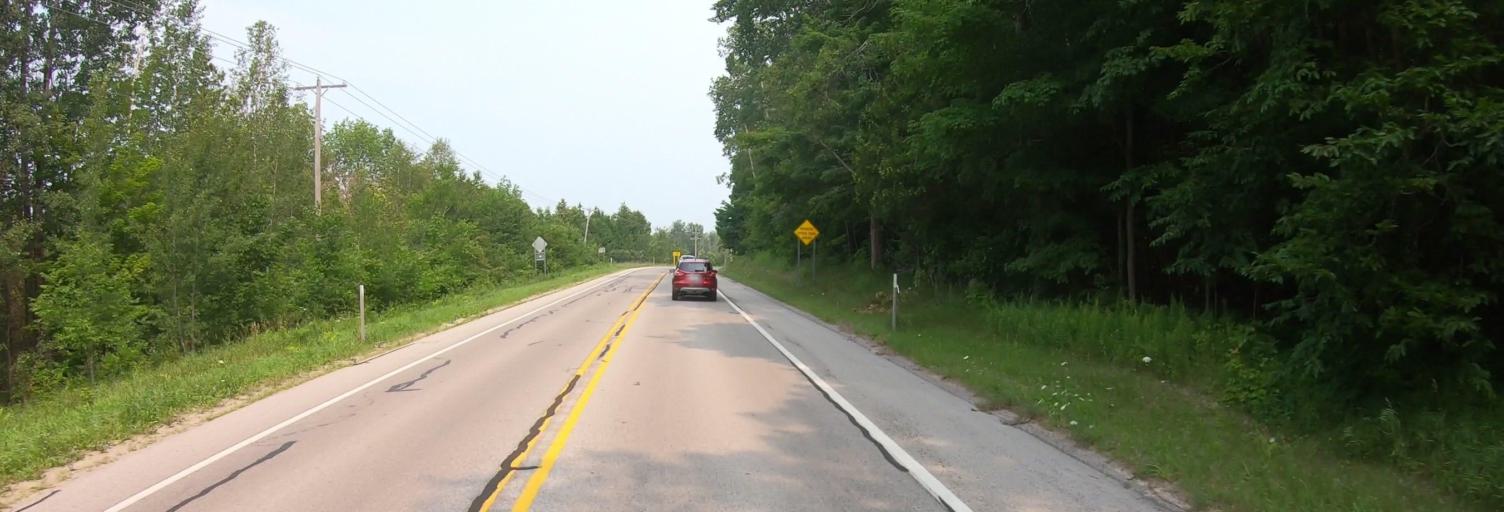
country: US
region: Michigan
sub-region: Leelanau County
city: Leland
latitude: 45.1152
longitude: -85.6308
